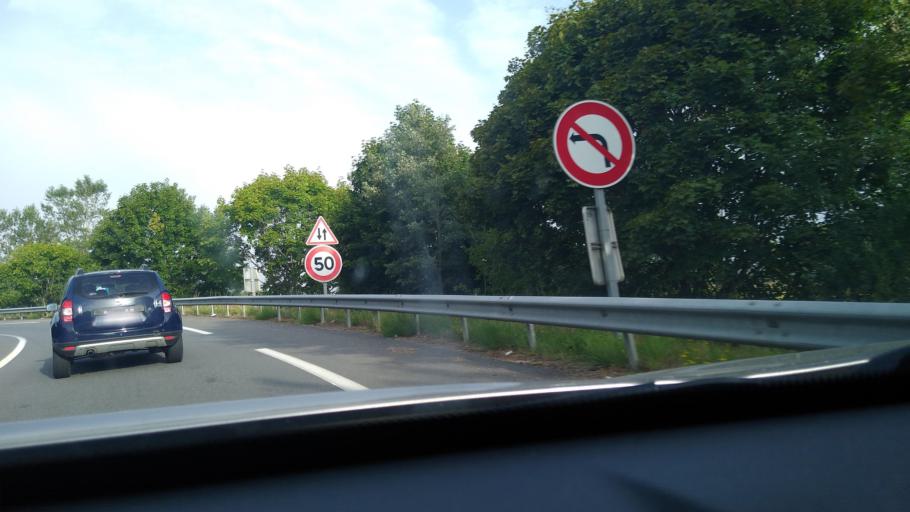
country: FR
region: Midi-Pyrenees
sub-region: Departement de la Haute-Garonne
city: Salies-du-Salat
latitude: 43.1299
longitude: 0.9428
